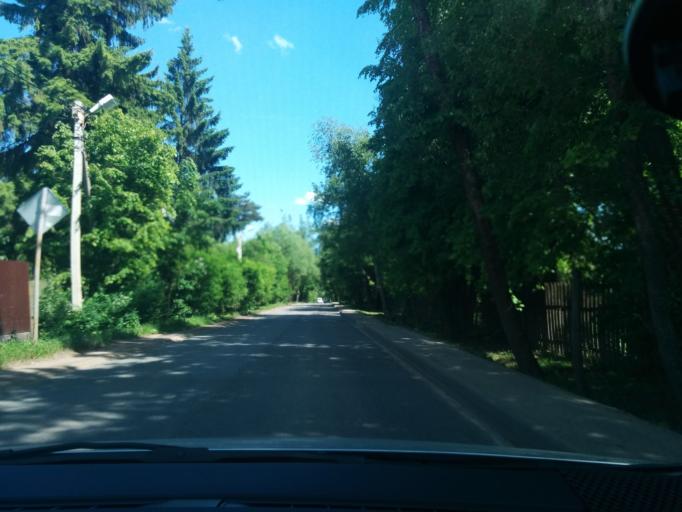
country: RU
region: Moskovskaya
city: Lugovaya
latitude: 56.0503
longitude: 37.5068
